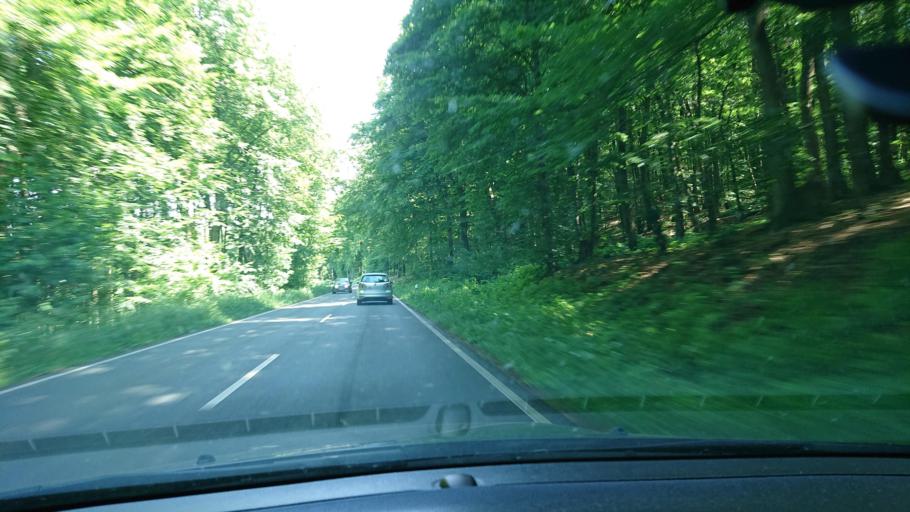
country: DE
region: North Rhine-Westphalia
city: Preussisch Oldendorf
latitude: 52.2902
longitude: 8.4620
